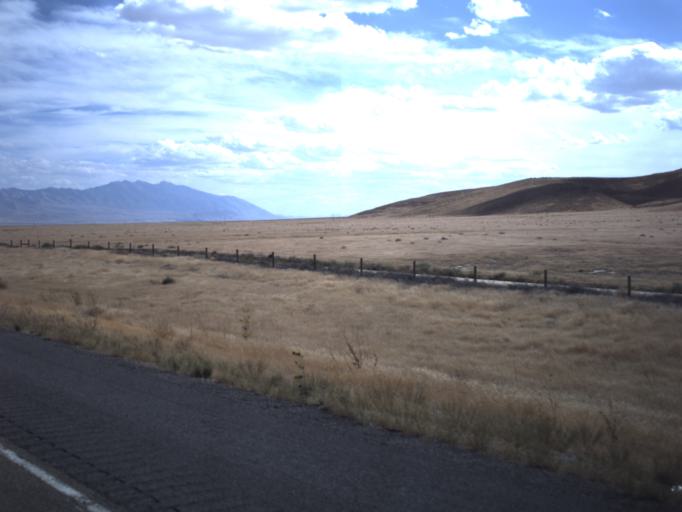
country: US
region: Utah
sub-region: Tooele County
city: Grantsville
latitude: 40.8089
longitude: -112.8660
